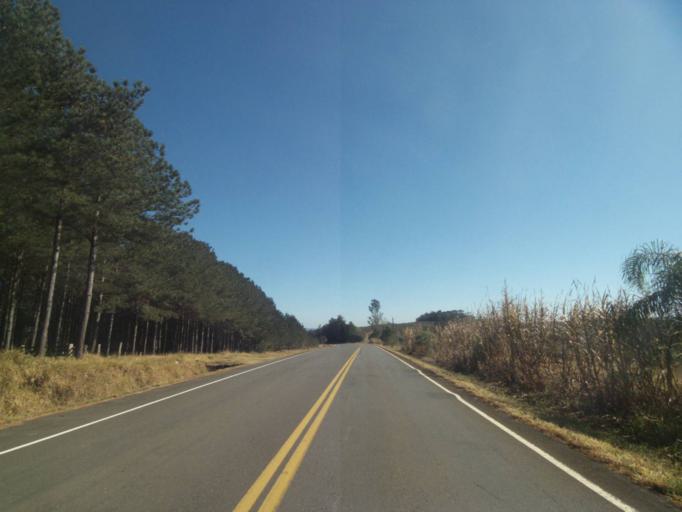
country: BR
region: Parana
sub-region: Telemaco Borba
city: Telemaco Borba
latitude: -24.4329
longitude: -50.5572
